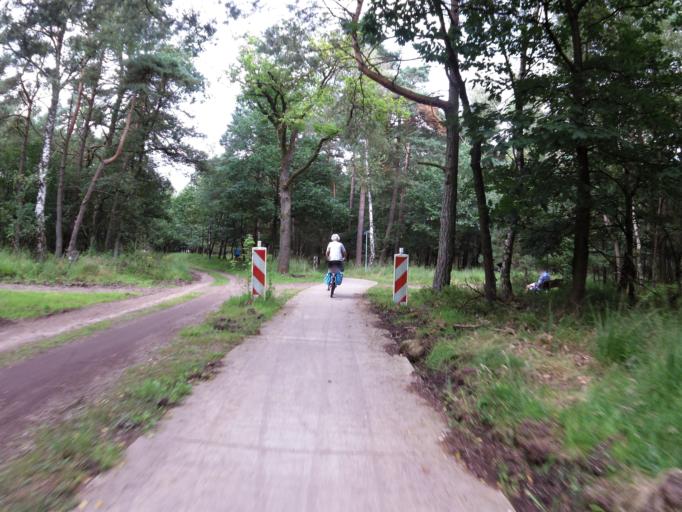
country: NL
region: Gelderland
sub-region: Gemeente Brummen
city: Eerbeek
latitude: 52.0695
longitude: 6.0291
